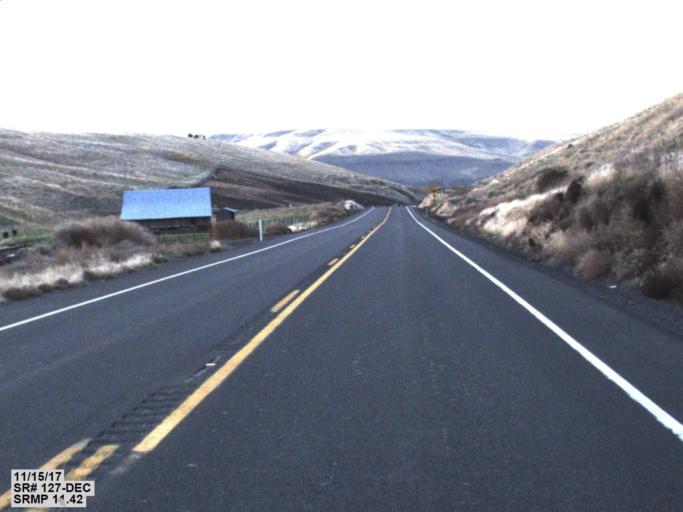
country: US
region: Washington
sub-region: Garfield County
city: Pomeroy
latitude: 46.6458
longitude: -117.8091
